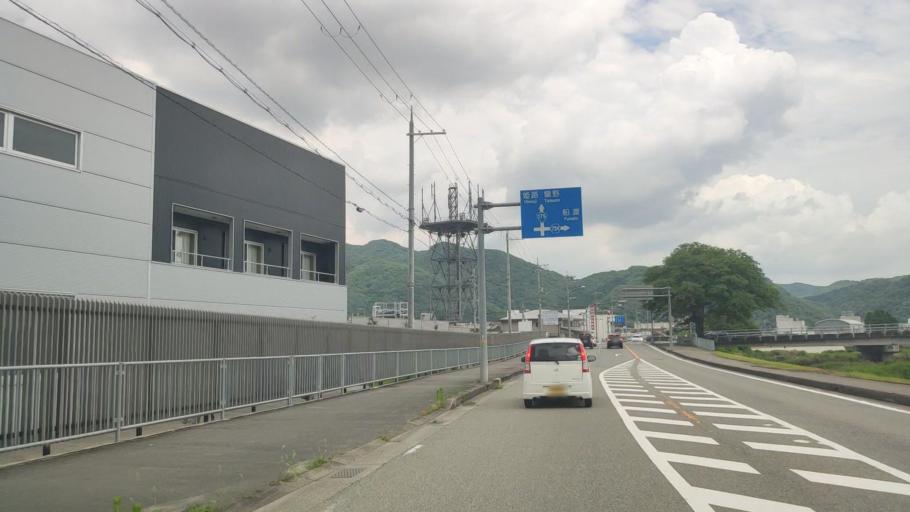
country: JP
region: Hyogo
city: Tatsunocho-tominaga
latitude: 34.9211
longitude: 134.5418
